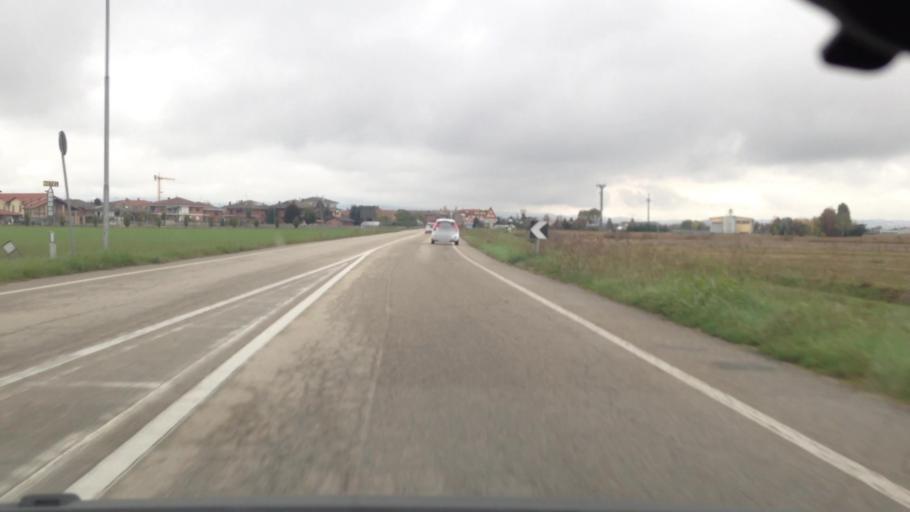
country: IT
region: Piedmont
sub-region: Provincia di Torino
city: Riva Presso Chieri
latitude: 44.9766
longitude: 7.8822
